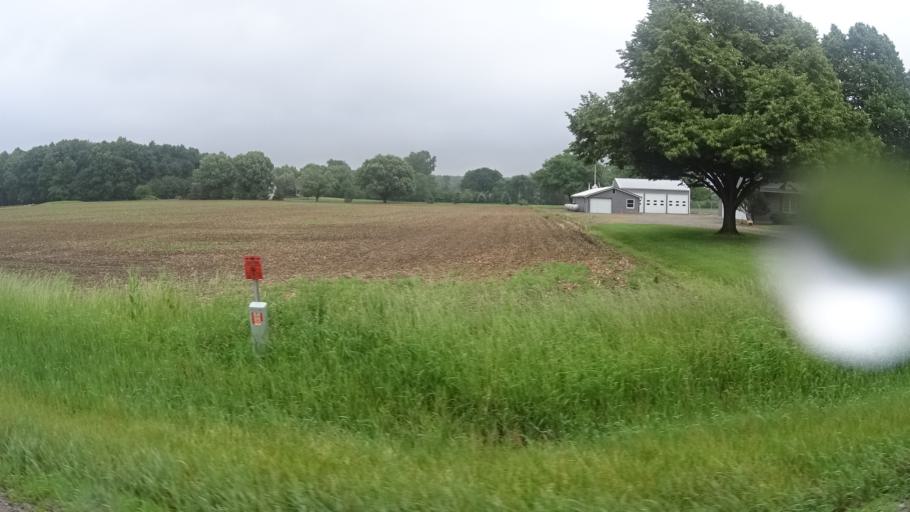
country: US
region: Ohio
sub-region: Huron County
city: Bellevue
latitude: 41.3280
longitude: -82.8298
